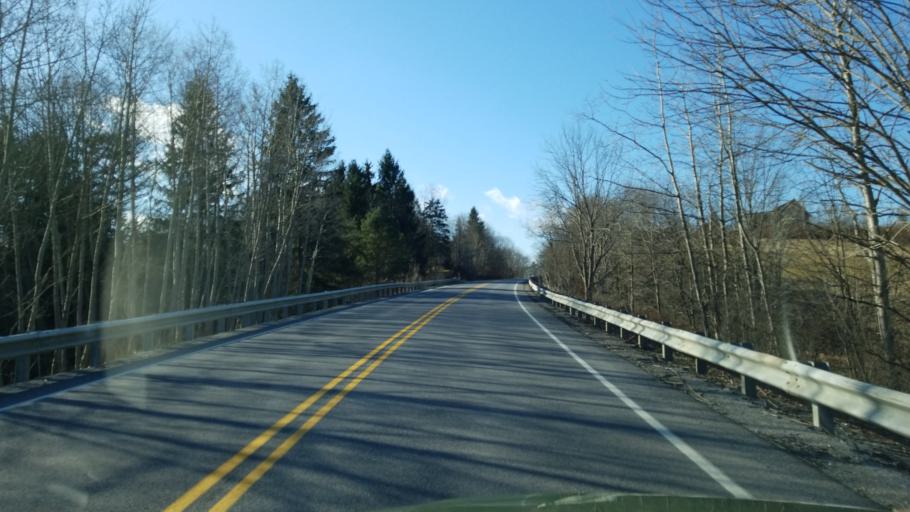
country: US
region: Pennsylvania
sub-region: Clearfield County
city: Hyde
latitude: 40.9836
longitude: -78.4463
